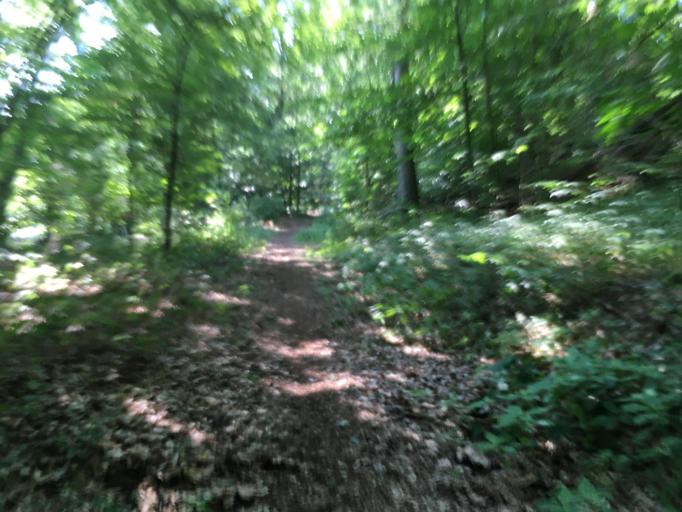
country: DE
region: Brandenburg
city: Templin
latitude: 53.1251
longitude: 13.5662
